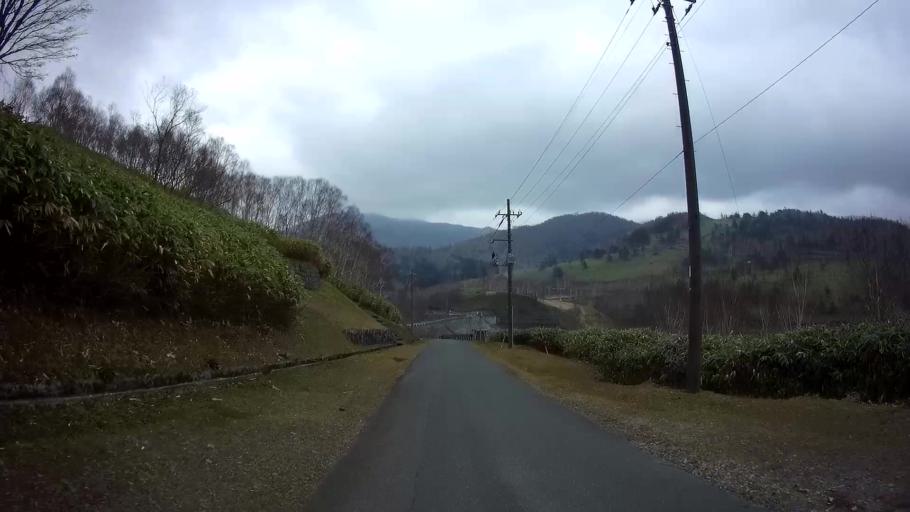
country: JP
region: Gunma
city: Nakanojomachi
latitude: 36.7173
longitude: 138.6402
